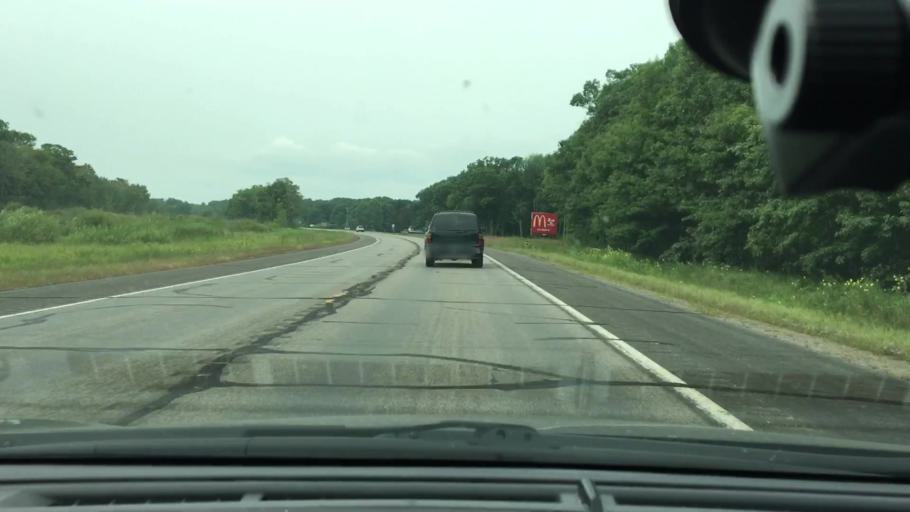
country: US
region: Minnesota
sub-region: Mille Lacs County
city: Vineland
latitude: 46.3238
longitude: -93.7978
